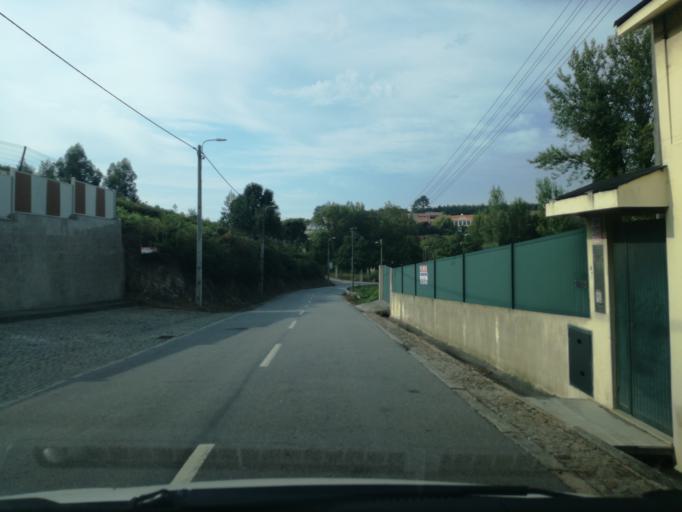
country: PT
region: Porto
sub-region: Vila Nova de Gaia
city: Sao Felix da Marinha
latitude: 41.0312
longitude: -8.6303
